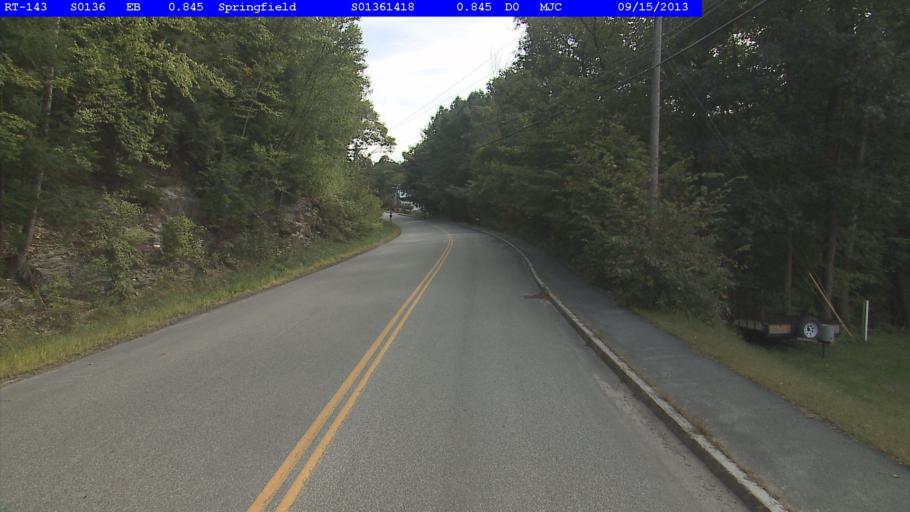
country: US
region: Vermont
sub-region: Windsor County
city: Springfield
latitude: 43.2950
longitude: -72.4684
